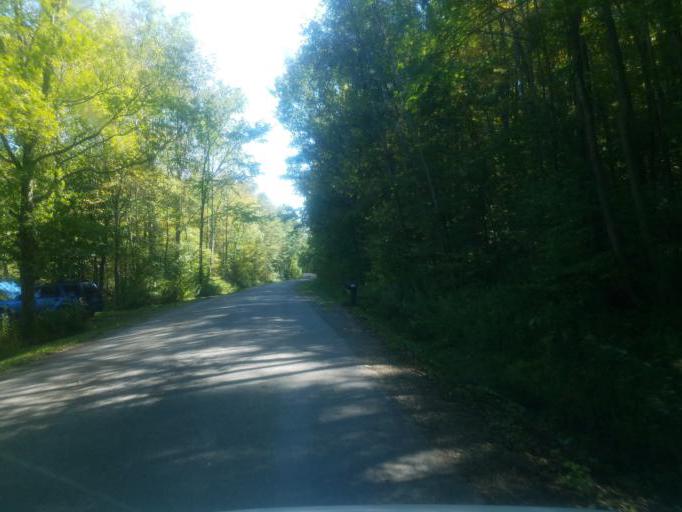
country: US
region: New York
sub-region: Allegany County
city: Cuba
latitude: 42.3130
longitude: -78.2055
